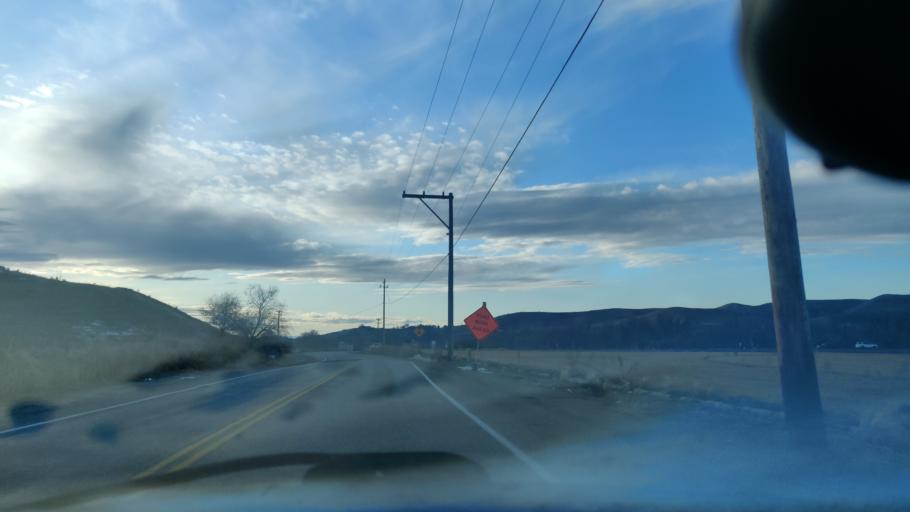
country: US
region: Idaho
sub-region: Ada County
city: Eagle
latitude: 43.7301
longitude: -116.3020
